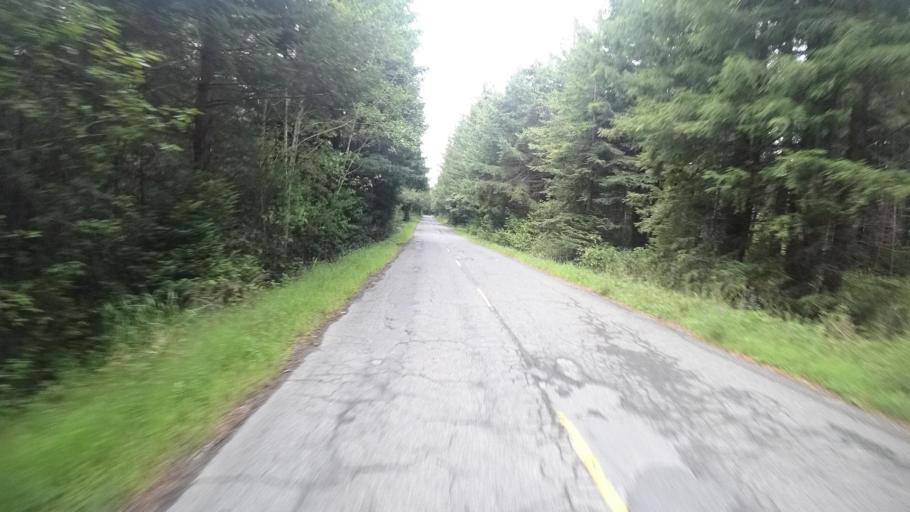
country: US
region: California
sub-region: Humboldt County
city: Blue Lake
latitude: 40.8755
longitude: -123.9693
